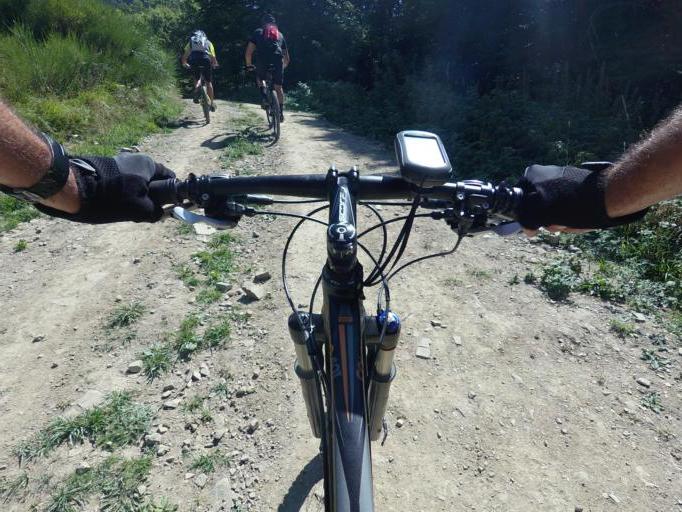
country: IT
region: Emilia-Romagna
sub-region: Provincia di Modena
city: Montecreto
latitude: 44.2234
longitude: 10.7180
